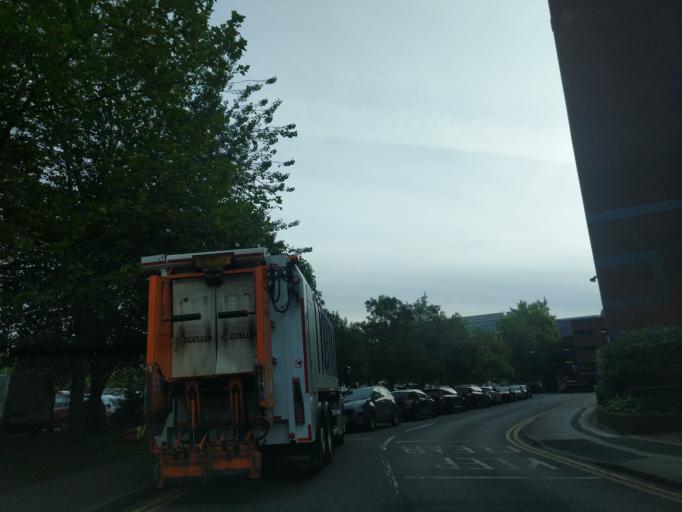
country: GB
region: England
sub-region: City and Borough of Leeds
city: Leeds
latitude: 53.7977
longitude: -1.5571
